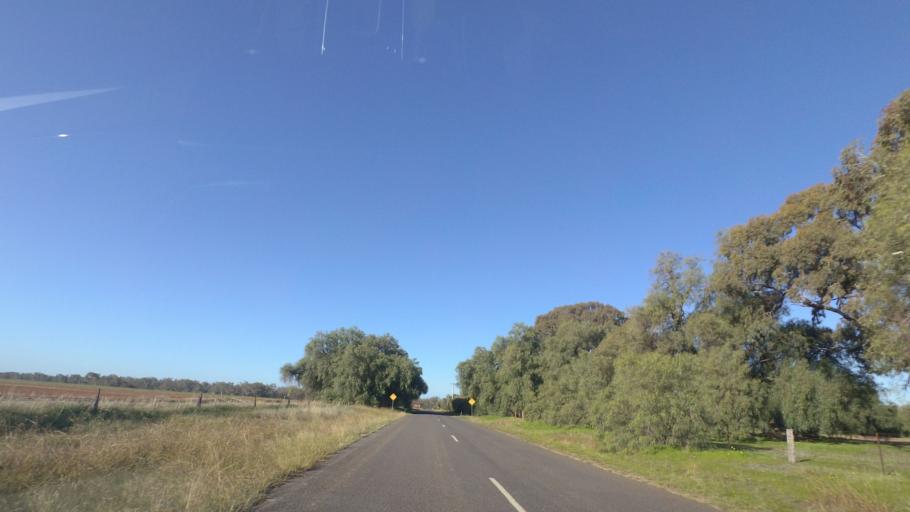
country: AU
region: Victoria
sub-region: Greater Bendigo
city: Epsom
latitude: -36.6464
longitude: 144.5359
